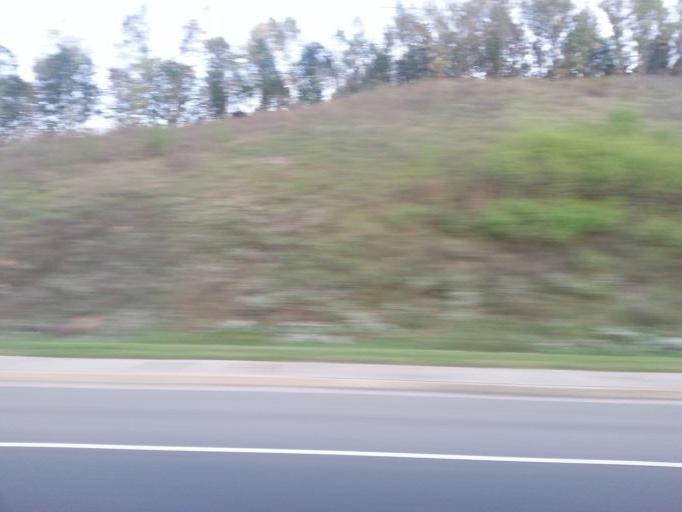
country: US
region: Tennessee
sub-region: Sevier County
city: Sevierville
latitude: 35.9012
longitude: -83.5810
